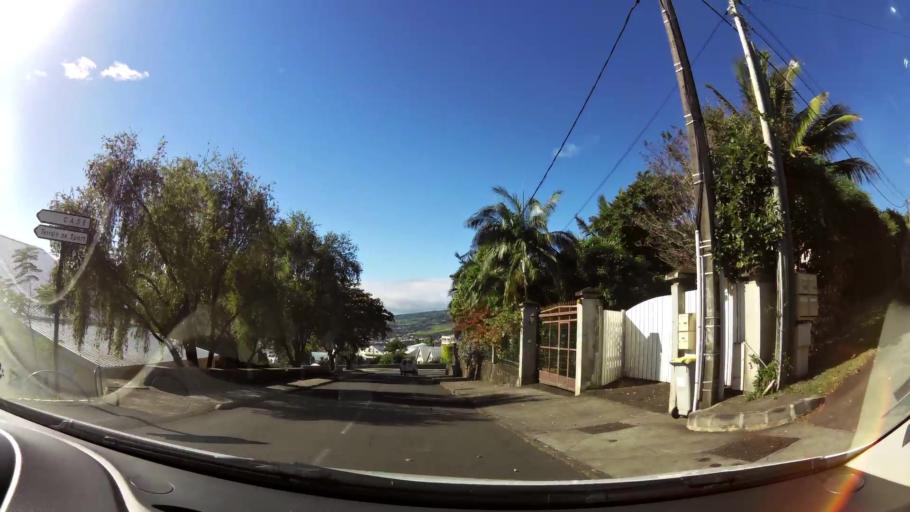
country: RE
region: Reunion
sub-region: Reunion
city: Saint-Denis
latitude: -20.9166
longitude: 55.4775
